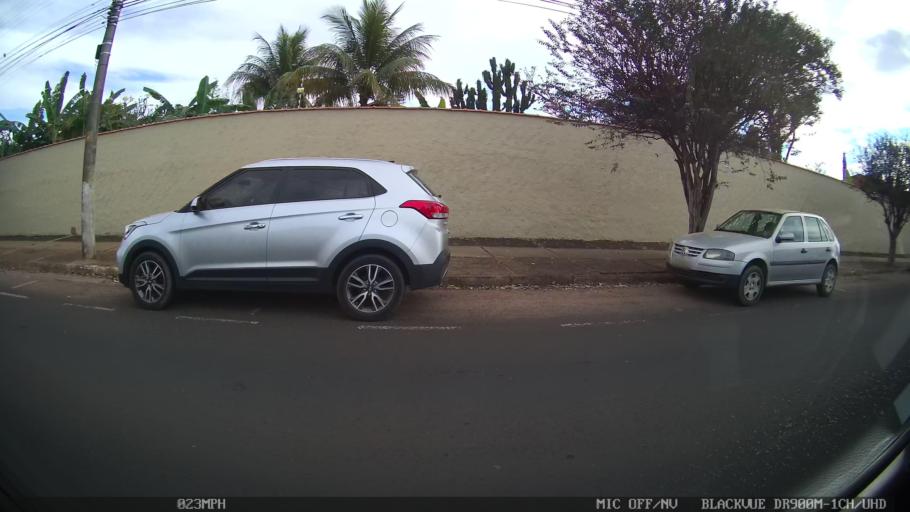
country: BR
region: Sao Paulo
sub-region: Catanduva
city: Catanduva
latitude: -21.1438
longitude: -48.9805
